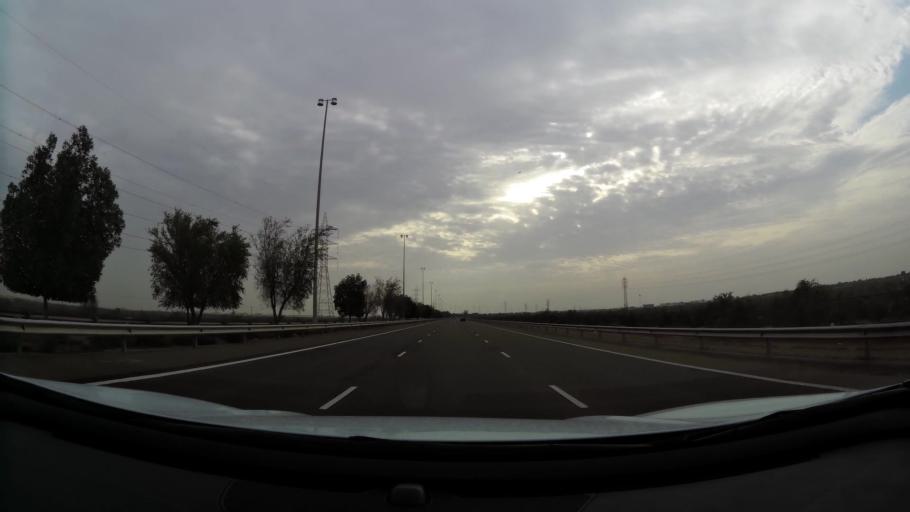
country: AE
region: Abu Dhabi
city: Abu Dhabi
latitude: 24.2157
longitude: 54.8765
